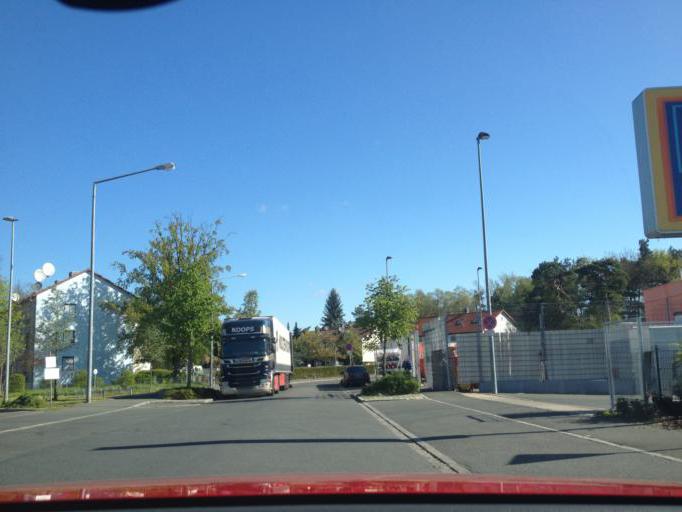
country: DE
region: Bavaria
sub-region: Regierungsbezirk Mittelfranken
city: Rothenbach an der Pegnitz
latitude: 49.4799
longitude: 11.2260
